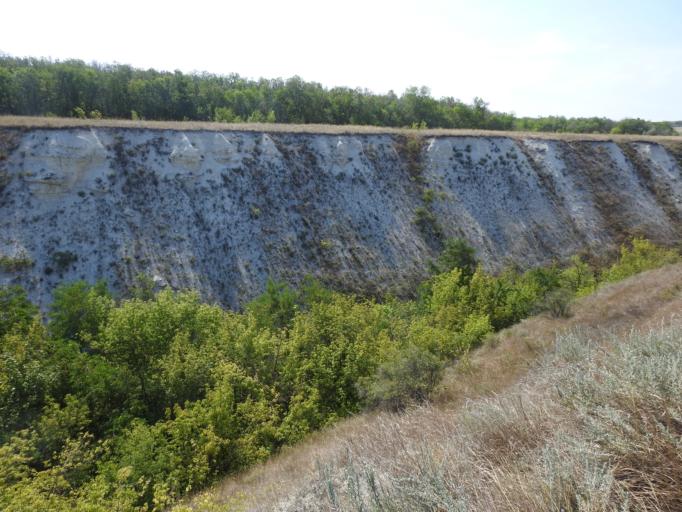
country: RU
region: Saratov
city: Kamenskiy
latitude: 50.6150
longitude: 45.6547
